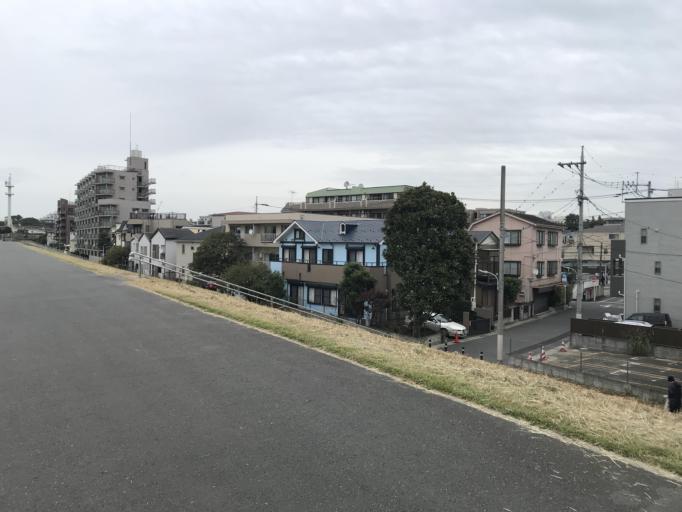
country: JP
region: Kanagawa
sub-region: Kawasaki-shi
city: Kawasaki
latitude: 35.5787
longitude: 139.6737
